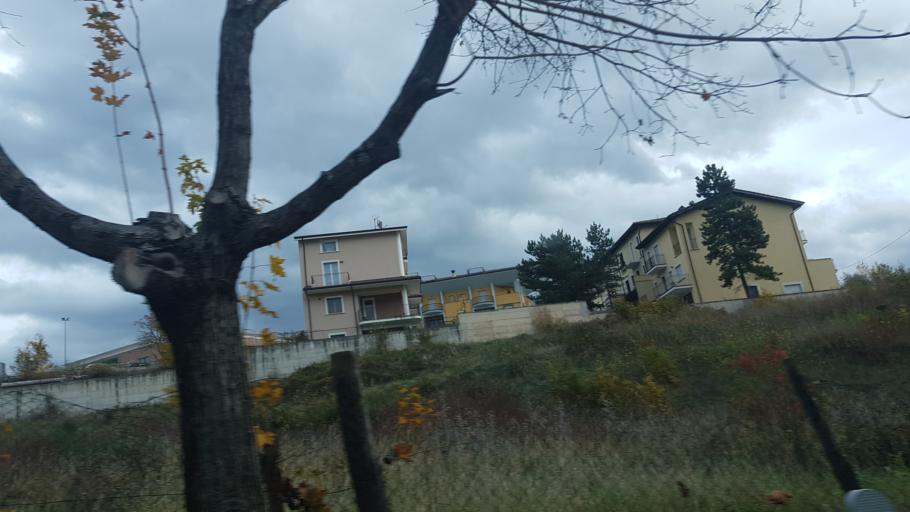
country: IT
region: Abruzzo
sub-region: Provincia dell' Aquila
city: L'Aquila
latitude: 42.3454
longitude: 13.4102
